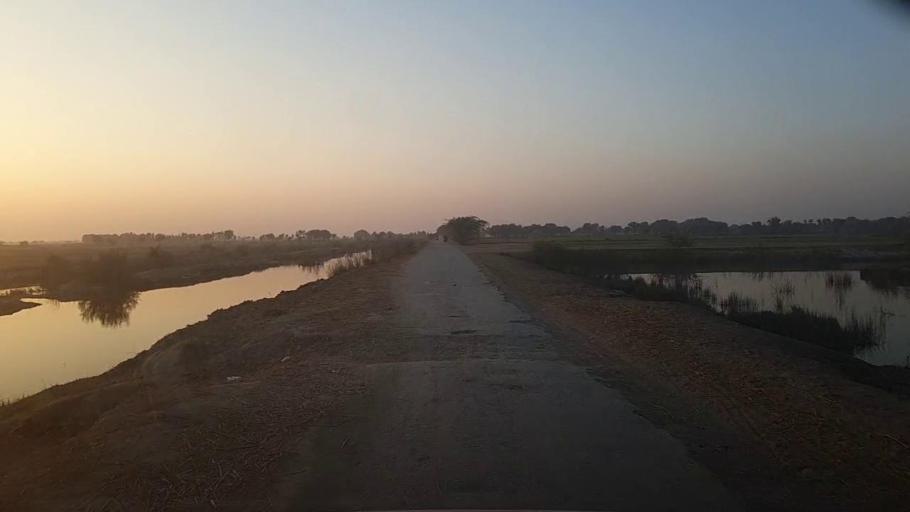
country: PK
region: Sindh
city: Khairpur Nathan Shah
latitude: 27.1557
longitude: 67.7228
